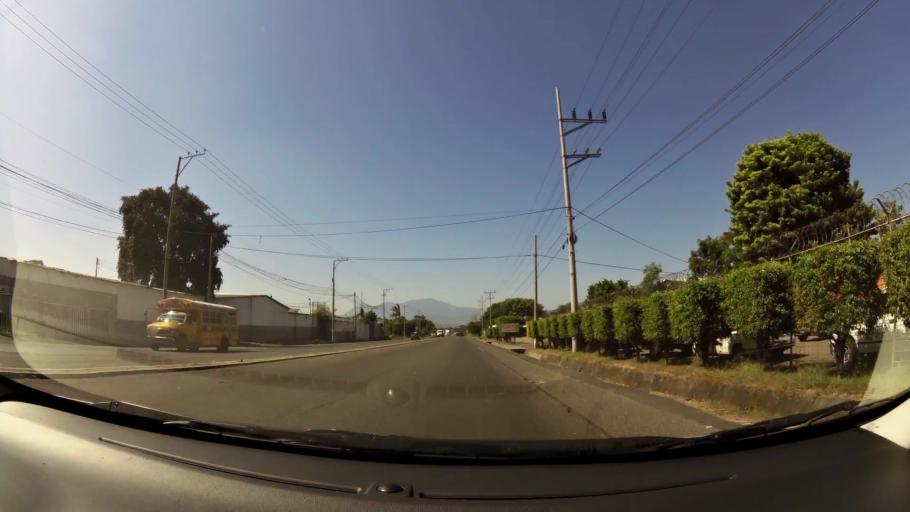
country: SV
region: La Libertad
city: Santa Tecla
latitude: 13.7301
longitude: -89.3827
